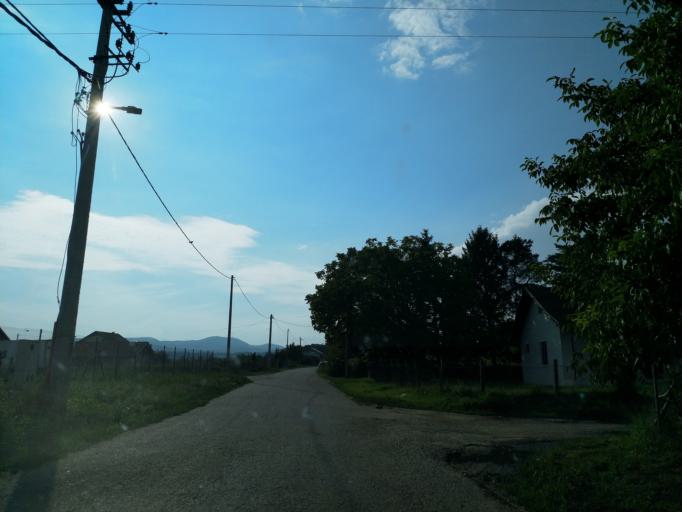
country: RS
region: Central Serbia
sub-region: Pomoravski Okrug
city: Jagodina
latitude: 43.9851
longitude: 21.2176
